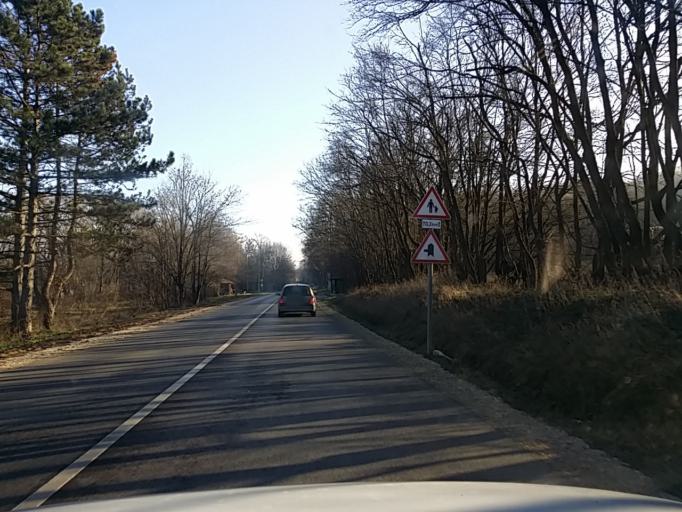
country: HU
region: Pest
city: Solymar
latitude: 47.5614
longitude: 18.9171
